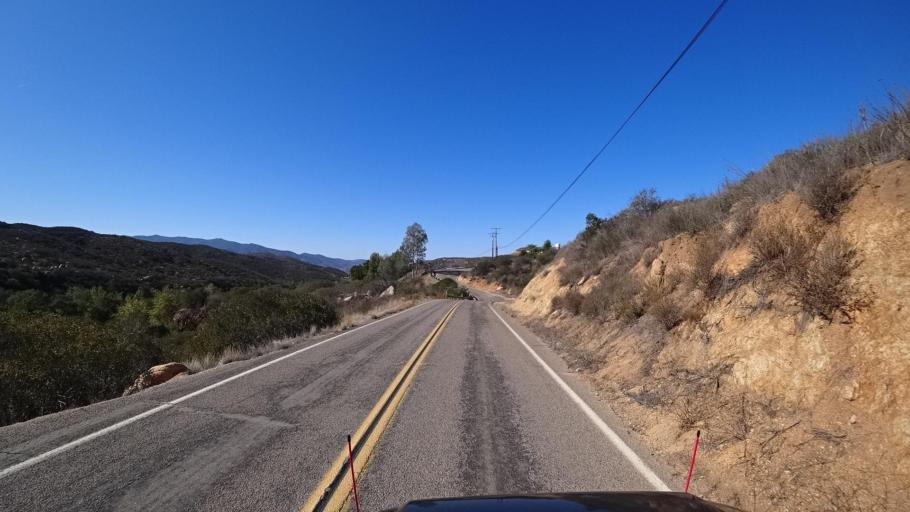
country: US
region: California
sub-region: San Diego County
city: Jamul
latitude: 32.7088
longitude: -116.7972
